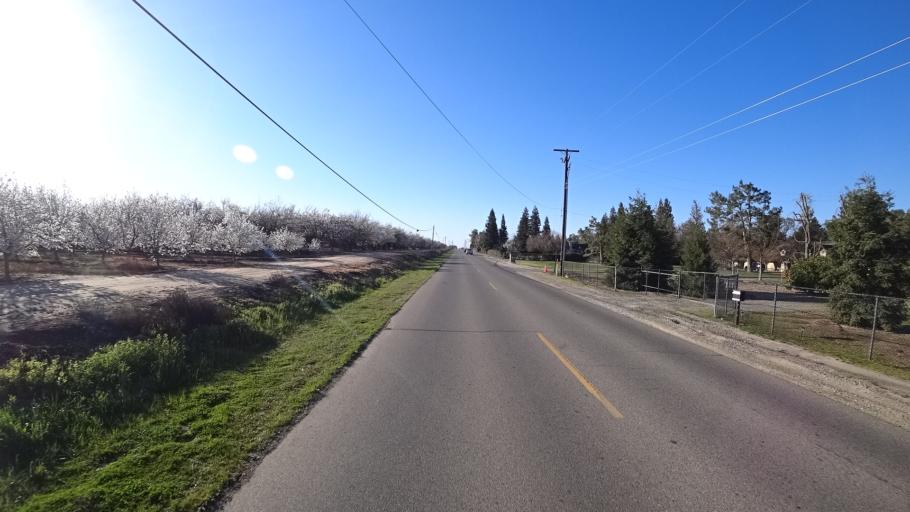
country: US
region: California
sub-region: Fresno County
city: Biola
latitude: 36.8046
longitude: -119.9164
